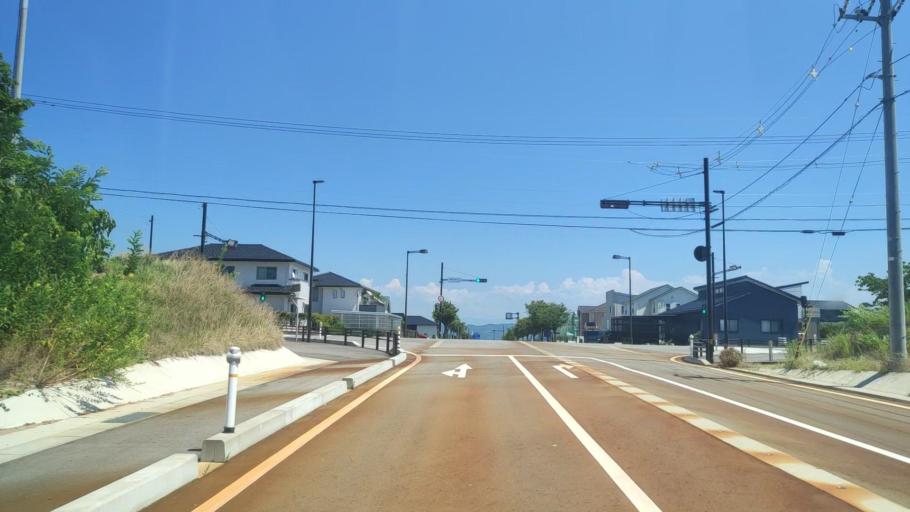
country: JP
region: Ishikawa
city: Kanazawa-shi
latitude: 36.6730
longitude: 136.6554
